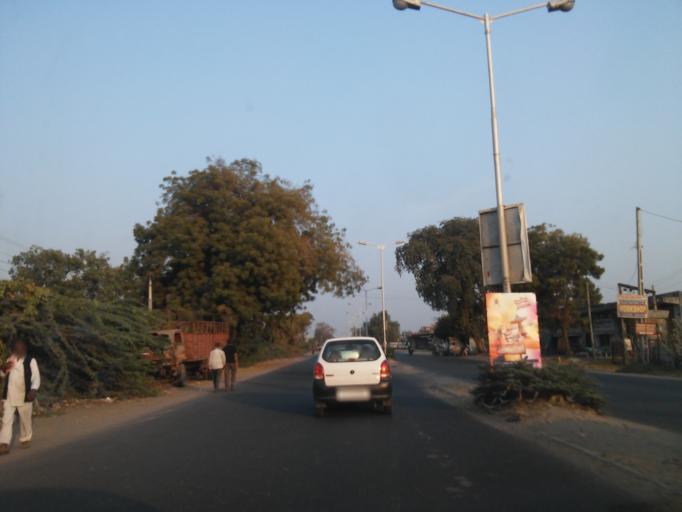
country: IN
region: Gujarat
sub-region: Ahmadabad
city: Sarkhej
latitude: 22.9875
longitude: 72.4851
